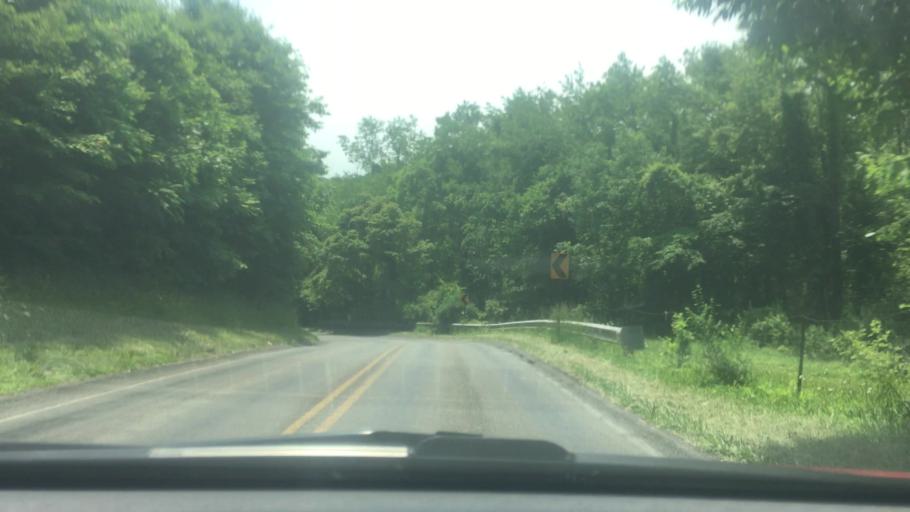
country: US
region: Pennsylvania
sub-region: Allegheny County
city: Bridgeville
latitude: 40.3436
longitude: -80.1490
